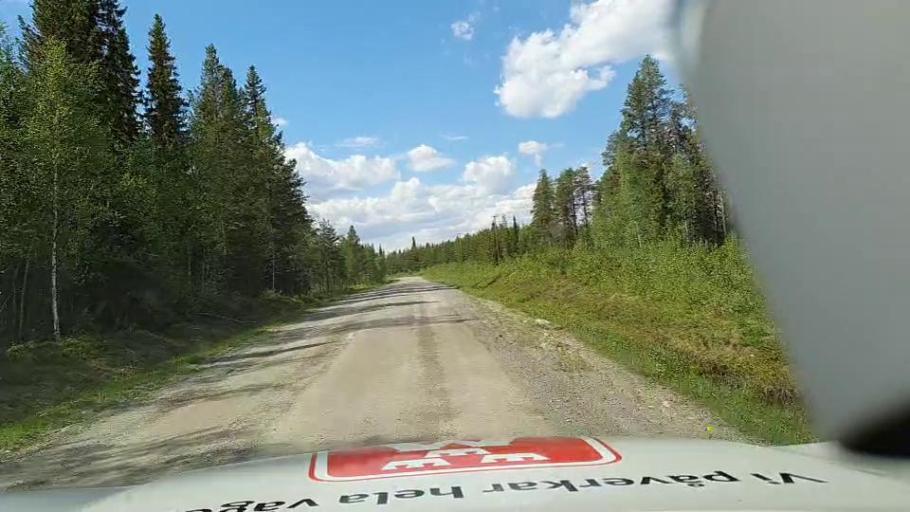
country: SE
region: Vaesterbotten
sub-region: Vilhelmina Kommun
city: Sjoberg
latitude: 64.5442
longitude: 15.6470
